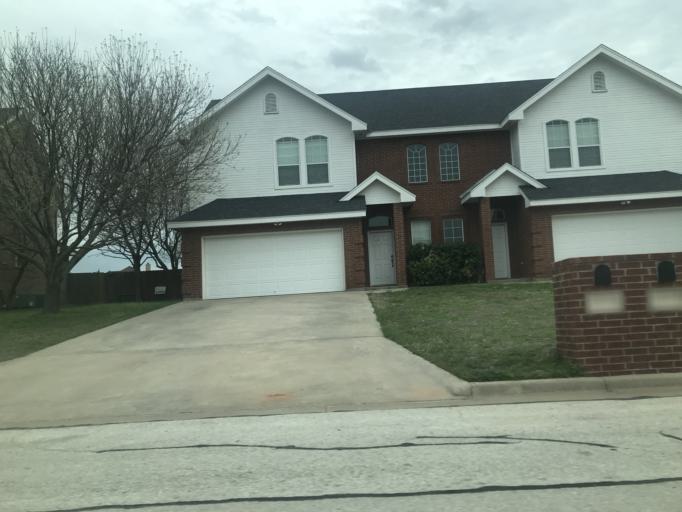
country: US
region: Texas
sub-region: Taylor County
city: Abilene
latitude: 32.4882
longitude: -99.6841
